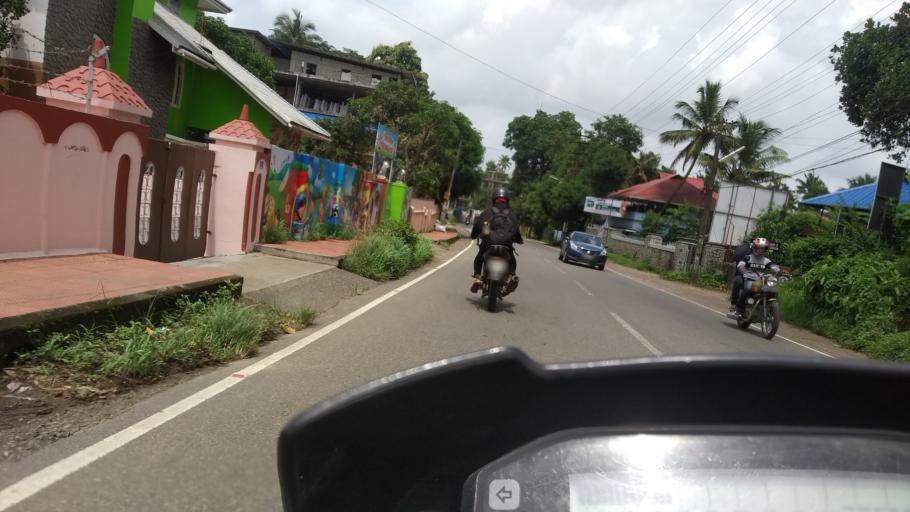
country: IN
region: Kerala
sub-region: Ernakulam
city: Aluva
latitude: 10.1218
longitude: 76.3362
